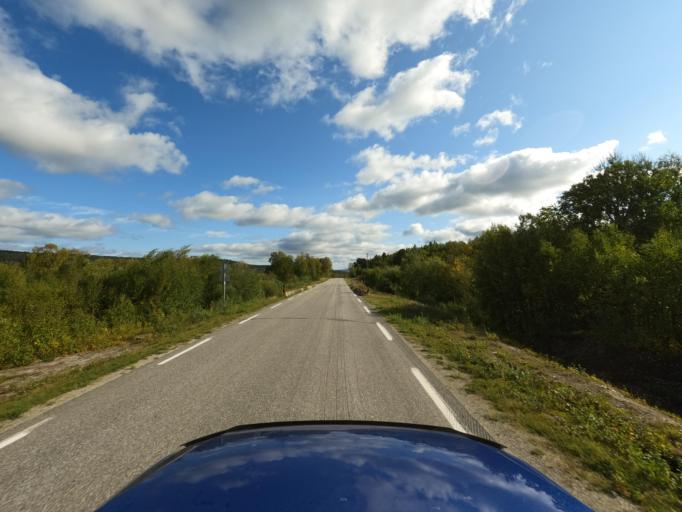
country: NO
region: Finnmark Fylke
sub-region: Karasjok
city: Karasjohka
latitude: 69.4484
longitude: 25.5973
